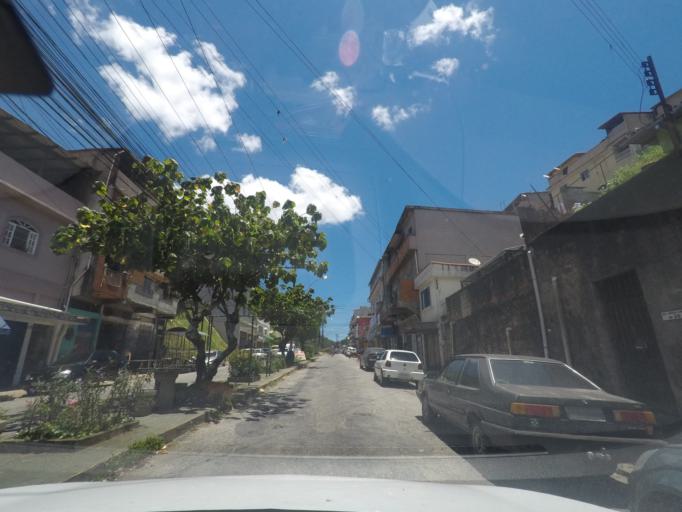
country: BR
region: Rio de Janeiro
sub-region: Teresopolis
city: Teresopolis
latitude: -22.4316
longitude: -42.9686
